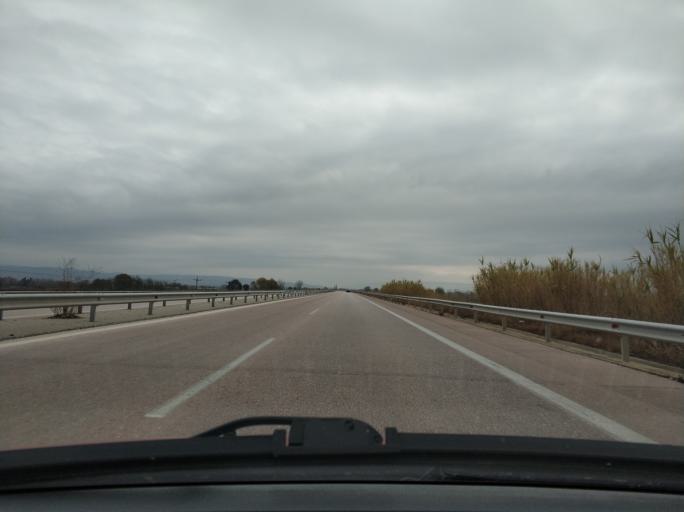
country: GR
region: Central Macedonia
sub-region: Nomos Thessalonikis
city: Lagkadas
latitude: 40.7287
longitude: 23.0649
